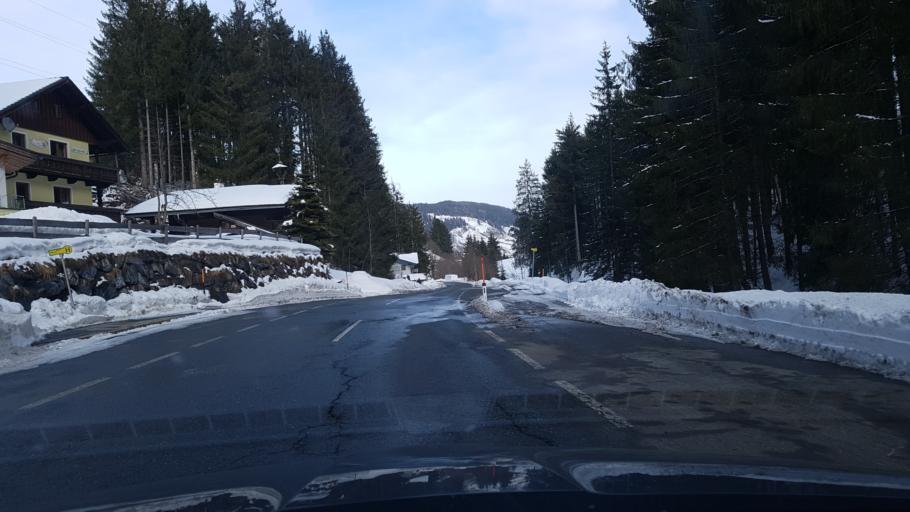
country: AT
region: Salzburg
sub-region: Politischer Bezirk Zell am See
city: Lend
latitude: 47.2936
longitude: 13.0128
